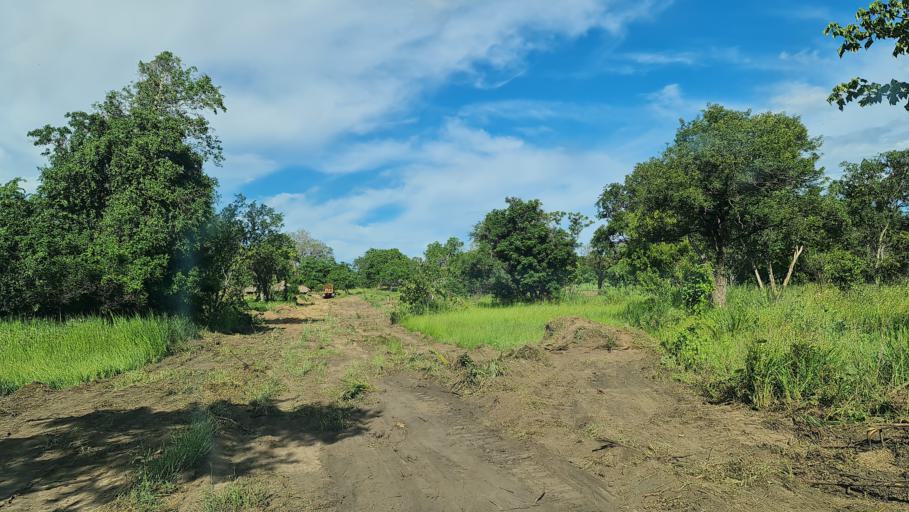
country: MZ
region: Nampula
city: Ilha de Mocambique
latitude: -15.5054
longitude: 40.1507
